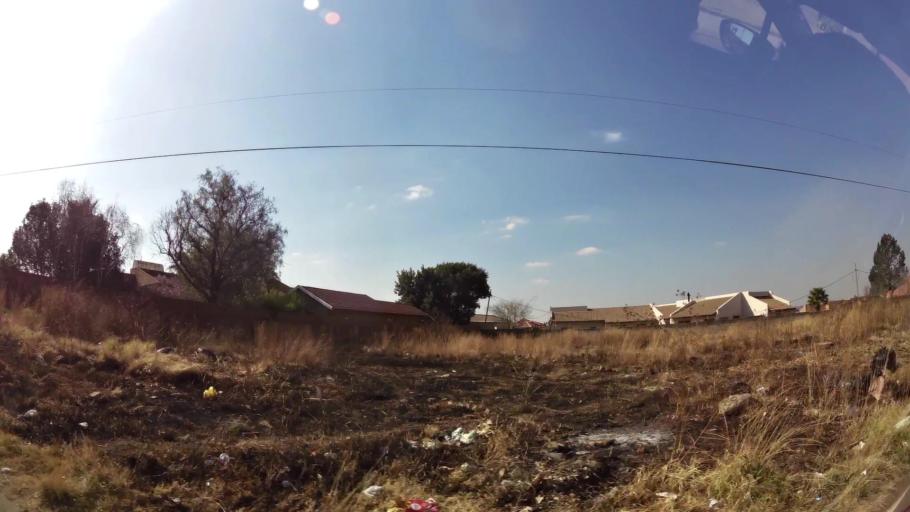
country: ZA
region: Gauteng
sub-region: City of Johannesburg Metropolitan Municipality
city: Roodepoort
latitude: -26.1677
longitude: 27.8031
